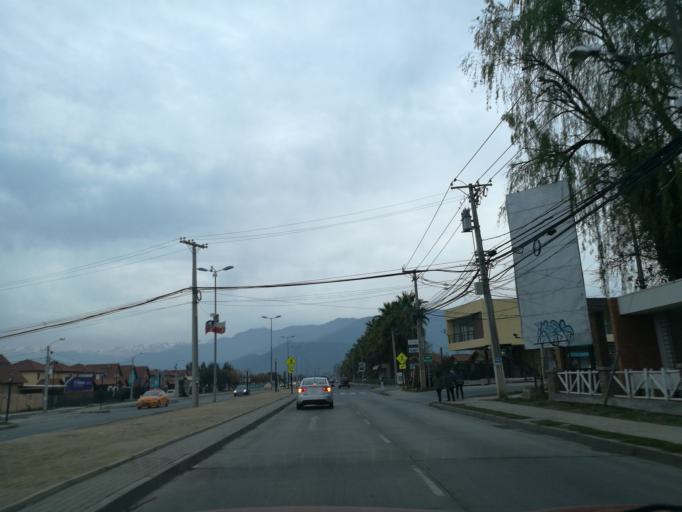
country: CL
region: O'Higgins
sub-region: Provincia de Cachapoal
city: Machali
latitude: -34.1713
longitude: -70.6824
